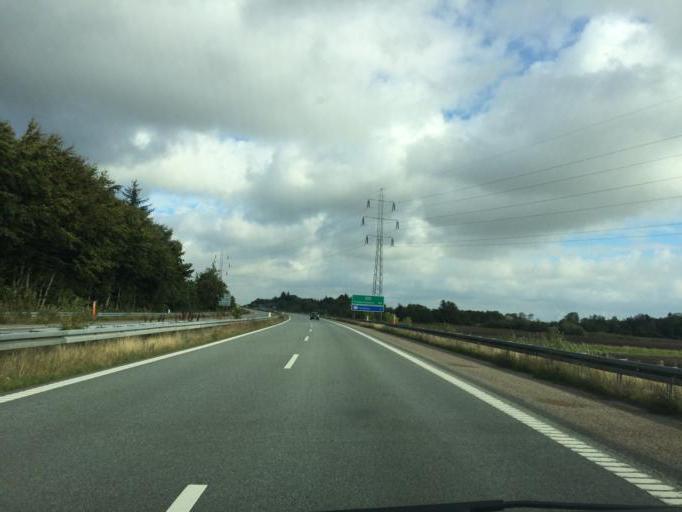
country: DK
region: North Denmark
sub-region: Alborg Kommune
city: Vodskov
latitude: 57.1188
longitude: 10.0665
